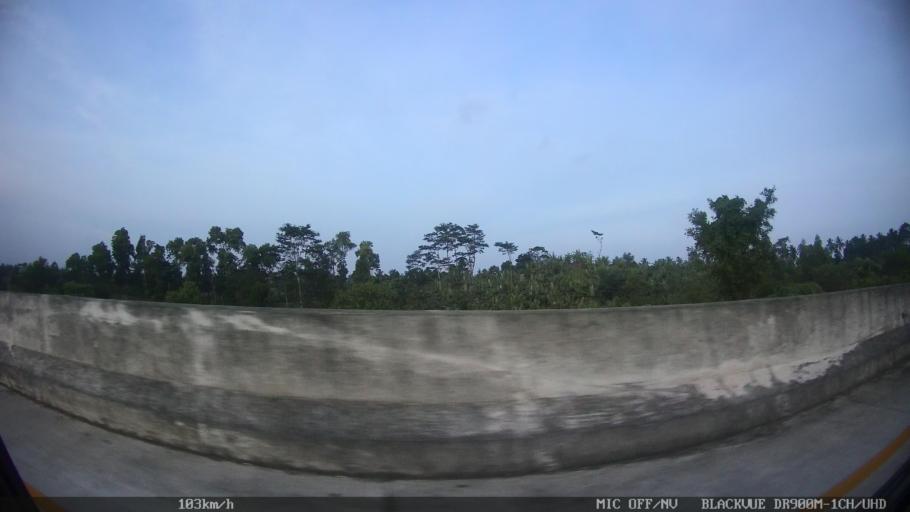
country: ID
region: Lampung
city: Penengahan
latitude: -5.7926
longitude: 105.7266
